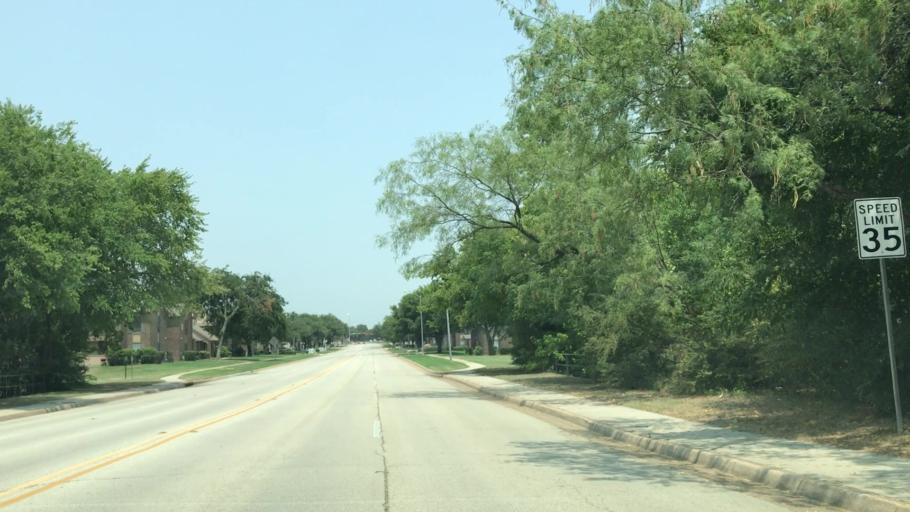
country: US
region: Texas
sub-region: Tarrant County
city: Euless
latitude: 32.8471
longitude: -97.0727
